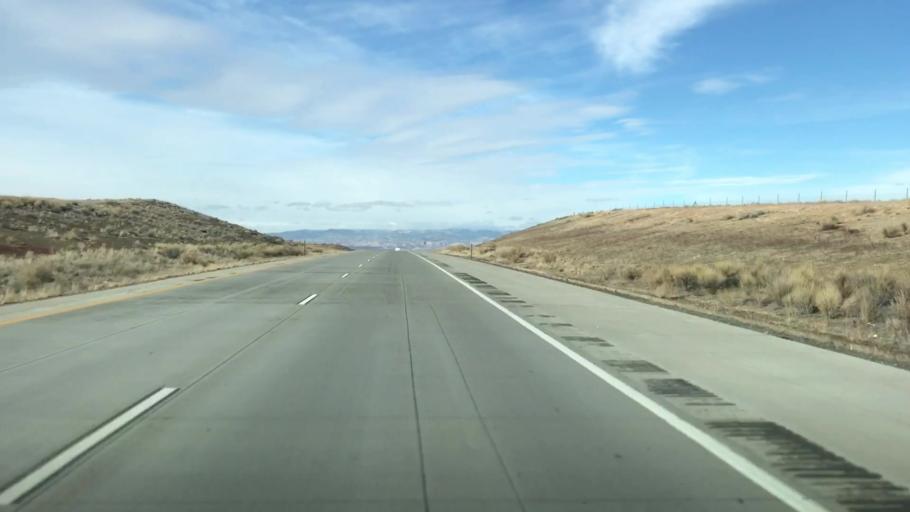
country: US
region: Colorado
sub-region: Mesa County
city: Loma
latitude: 39.1919
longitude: -108.8396
